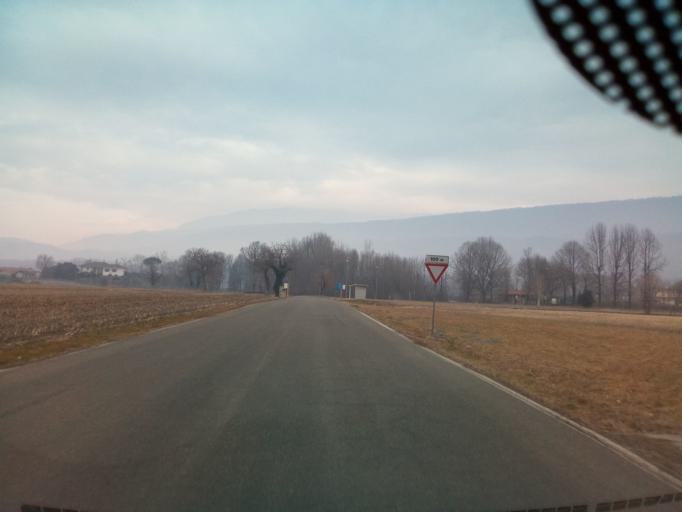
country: IT
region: Piedmont
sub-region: Provincia di Torino
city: Burolo
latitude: 45.4778
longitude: 7.9203
